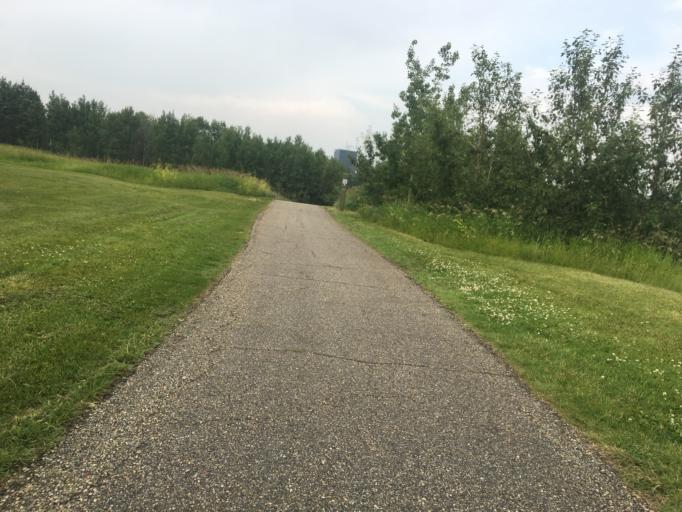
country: CA
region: Alberta
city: Grande Prairie
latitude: 55.1629
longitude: -118.8053
